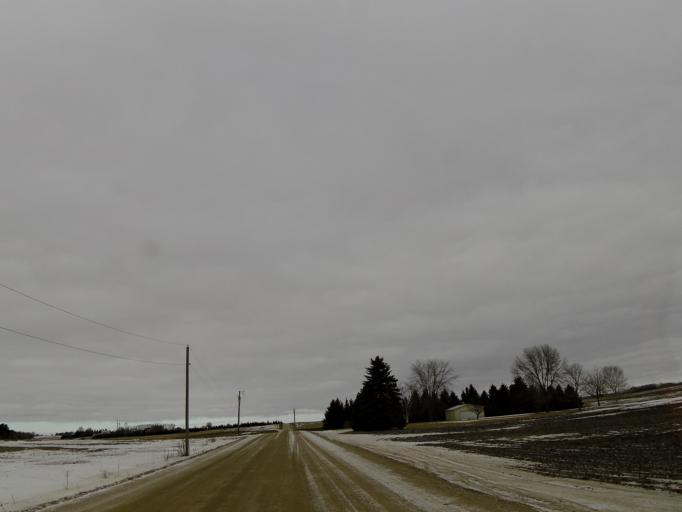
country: US
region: Minnesota
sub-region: Dakota County
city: Hastings
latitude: 44.8077
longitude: -92.8414
